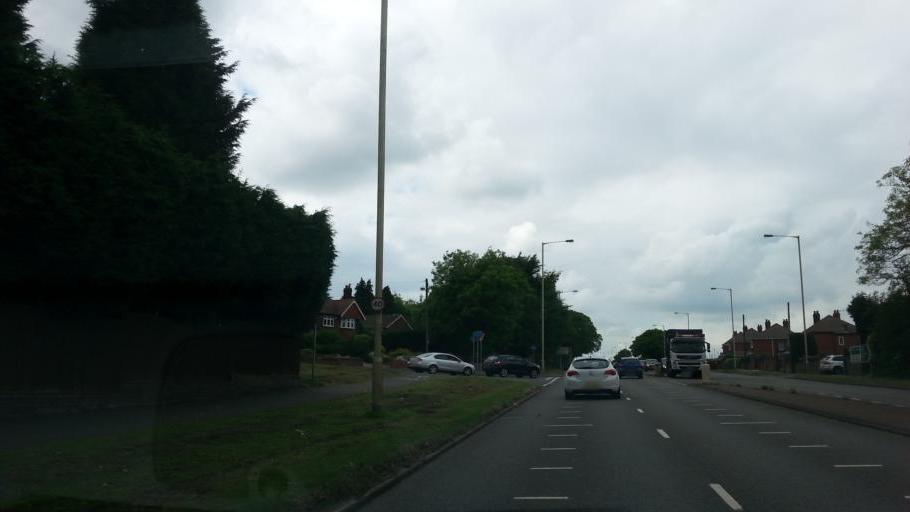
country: GB
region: England
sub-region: Sandwell
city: Tipton
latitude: 52.5358
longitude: -2.0877
